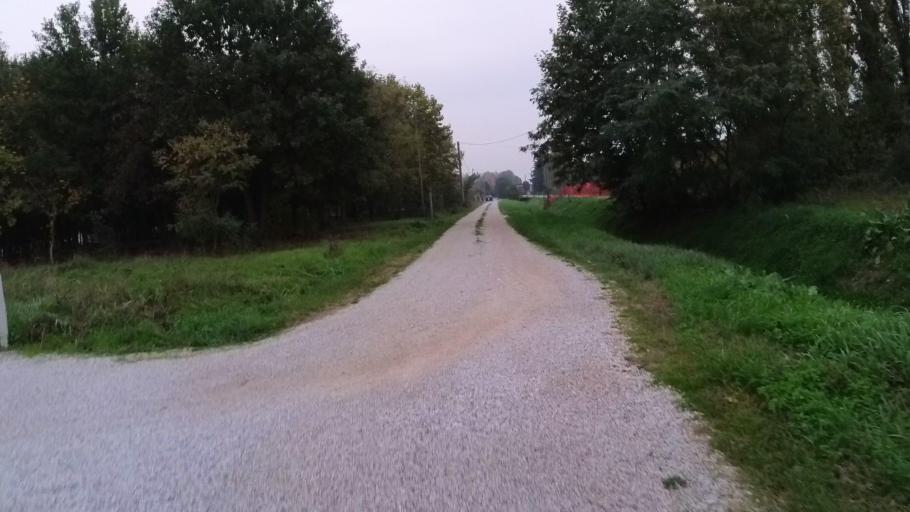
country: IT
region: Veneto
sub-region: Provincia di Padova
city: Bosco
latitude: 45.4411
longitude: 11.7901
